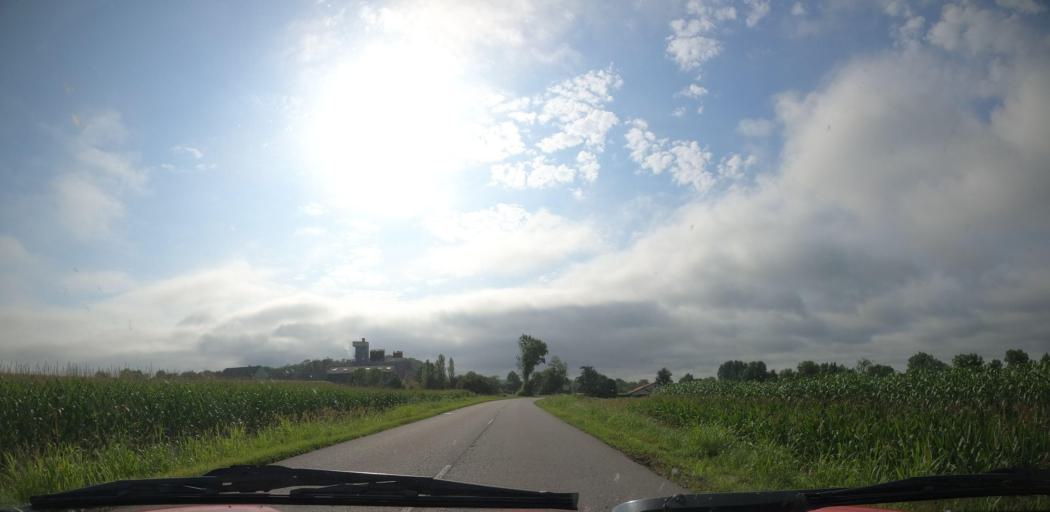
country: FR
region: Aquitaine
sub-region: Departement des Landes
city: Peyrehorade
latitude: 43.5350
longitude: -1.0709
